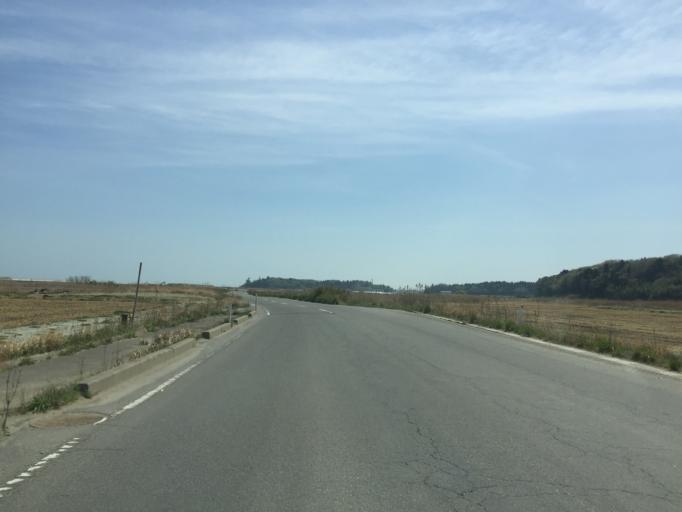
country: JP
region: Miyagi
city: Watari
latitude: 37.9116
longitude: 140.9194
